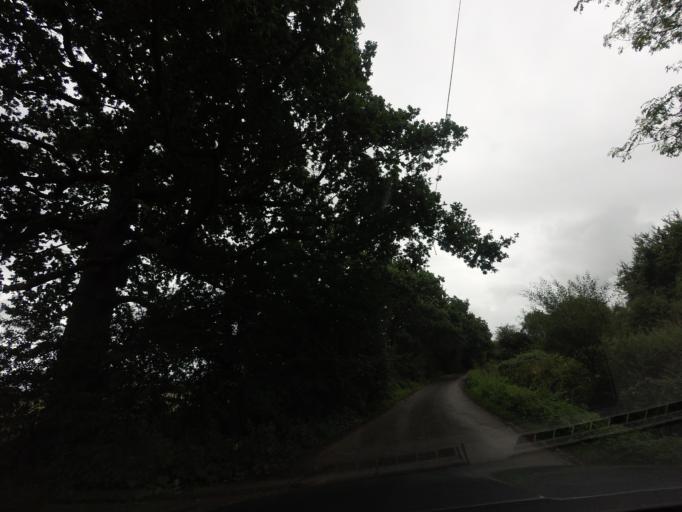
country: GB
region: England
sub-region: Kent
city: Paddock Wood
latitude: 51.1921
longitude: 0.4000
